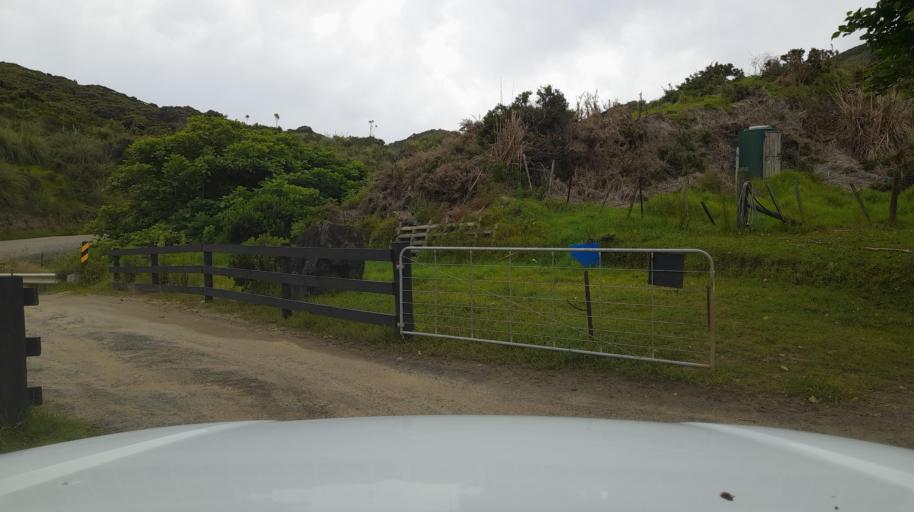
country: NZ
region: Northland
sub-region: Far North District
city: Ahipara
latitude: -35.1796
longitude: 173.1207
